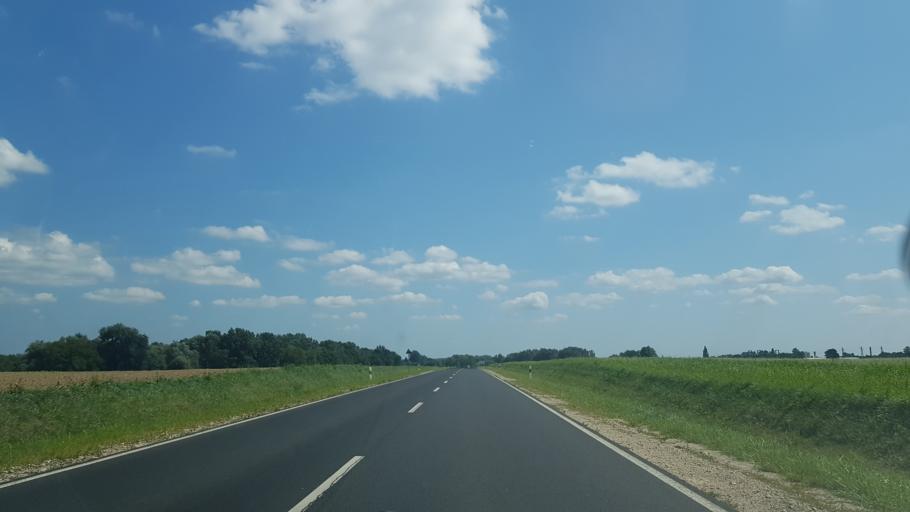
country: HU
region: Somogy
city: Marcali
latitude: 46.5962
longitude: 17.4254
